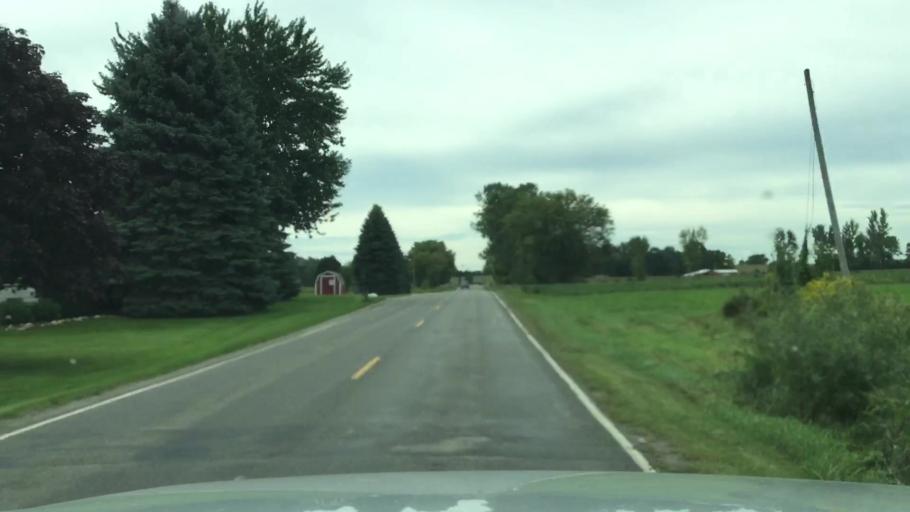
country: US
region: Michigan
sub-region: Shiawassee County
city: Durand
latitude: 42.9615
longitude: -83.9867
